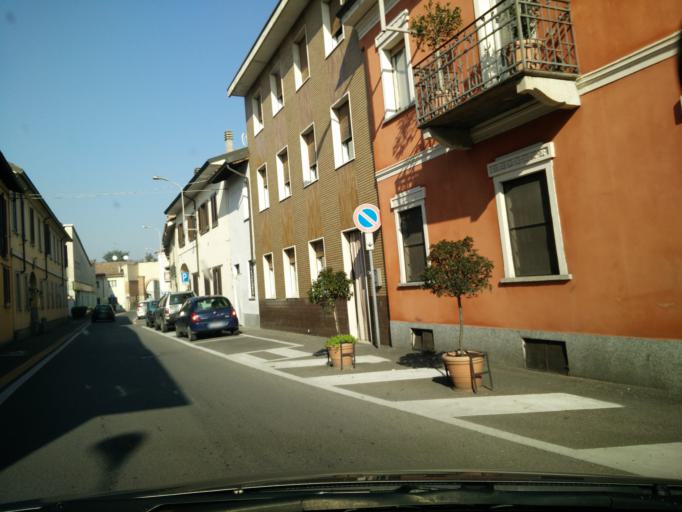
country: IT
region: Lombardy
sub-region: Provincia di Pavia
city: Sannazzaro de' Burgondi
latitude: 45.1031
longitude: 8.9109
